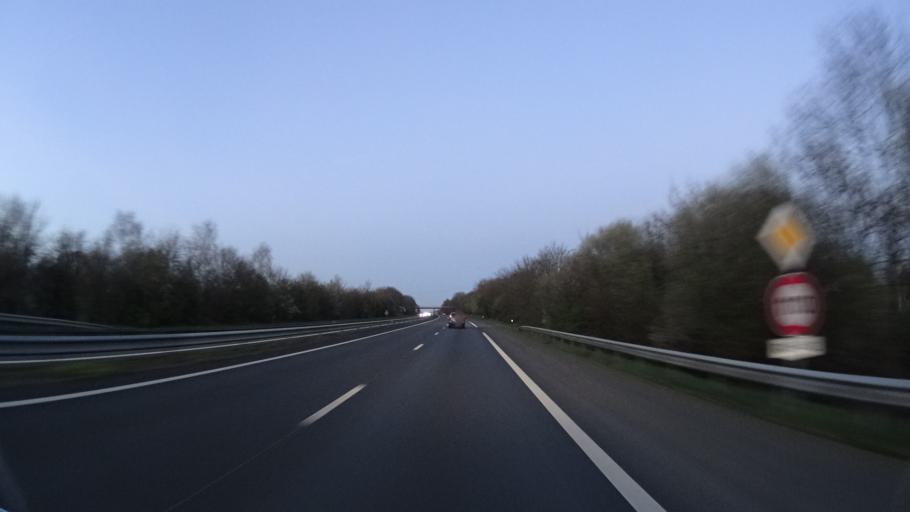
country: FR
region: Brittany
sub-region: Departement d'Ille-et-Vilaine
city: Mordelles
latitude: 48.0684
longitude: -1.8189
